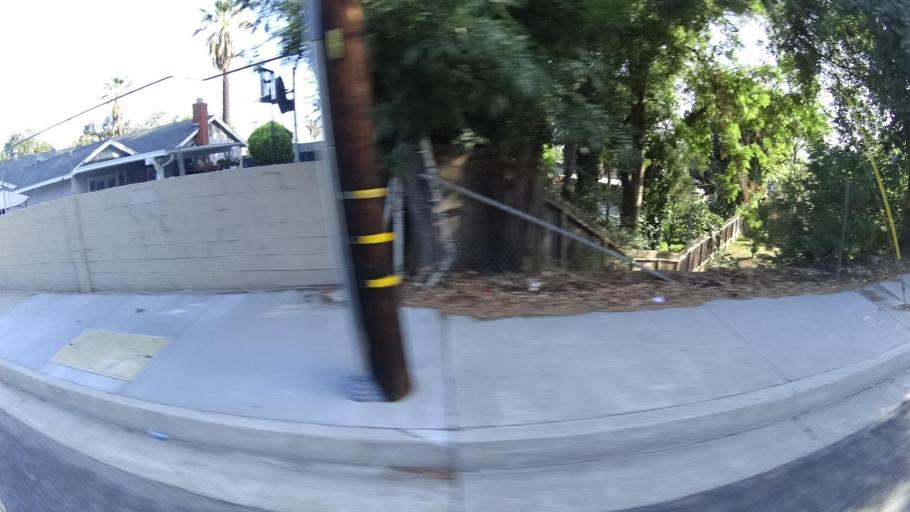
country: US
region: California
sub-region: Los Angeles County
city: La Puente
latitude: 34.0279
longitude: -117.9325
